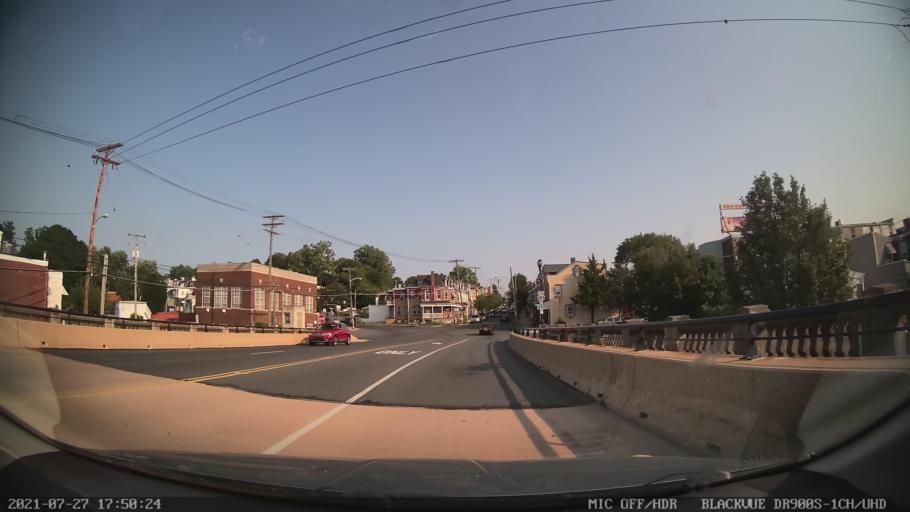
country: US
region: Pennsylvania
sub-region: Berks County
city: West Reading
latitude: 40.3498
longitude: -75.9429
